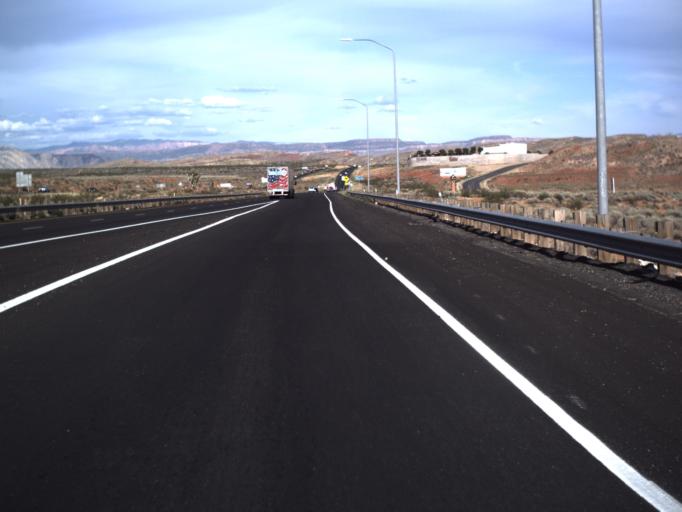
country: US
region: Utah
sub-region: Washington County
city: Washington
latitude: 37.1678
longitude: -113.4478
